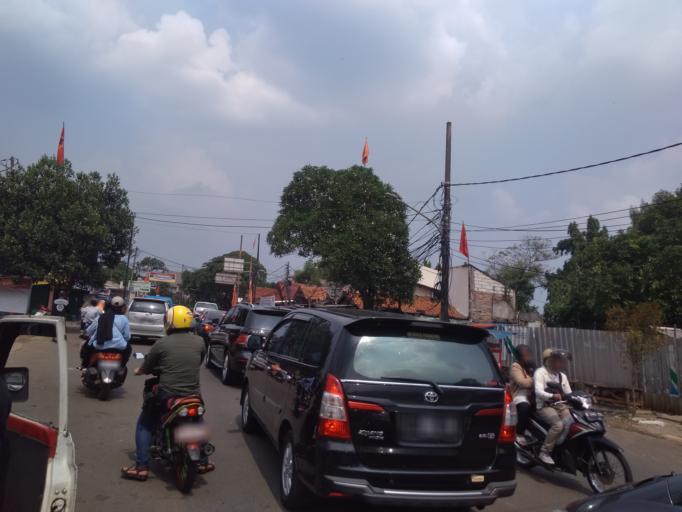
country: ID
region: Banten
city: South Tangerang
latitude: -6.2896
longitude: 106.7710
